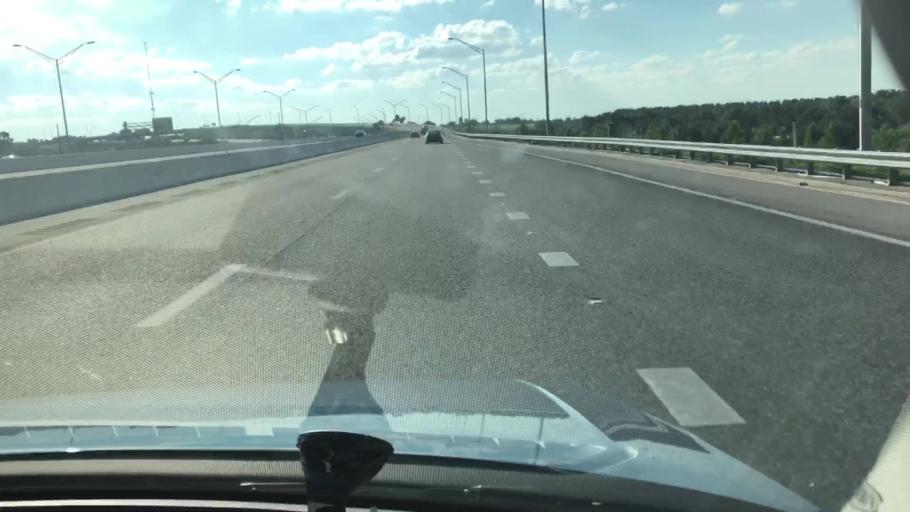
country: US
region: Florida
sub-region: Orange County
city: South Apopka
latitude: 28.6534
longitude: -81.5356
